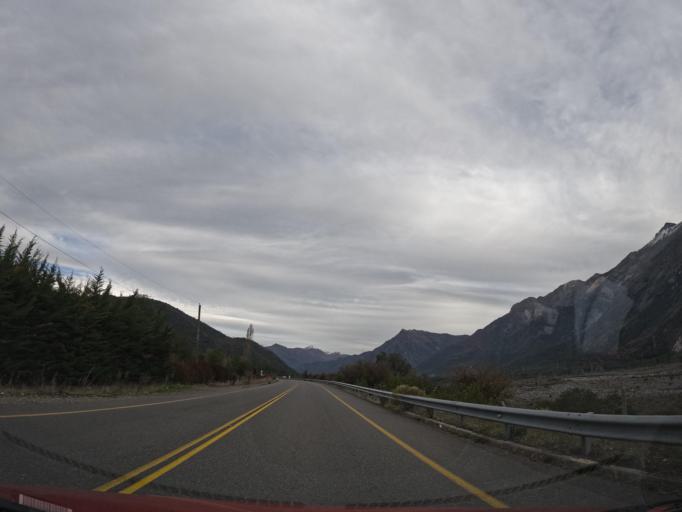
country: CL
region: Maule
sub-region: Provincia de Linares
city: Colbun
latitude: -35.7633
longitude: -71.0022
